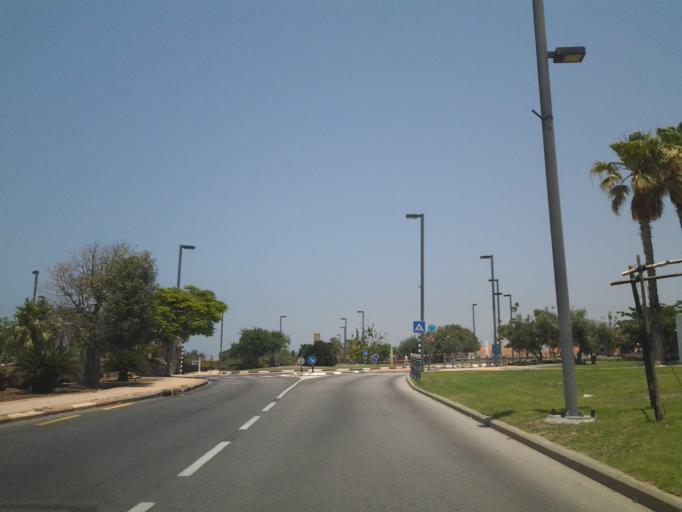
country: IL
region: Haifa
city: Qesarya
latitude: 32.5125
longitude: 34.9057
